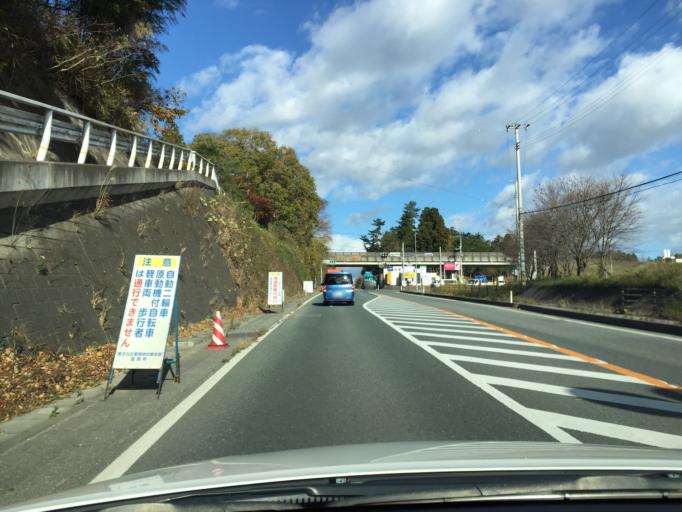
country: JP
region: Fukushima
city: Namie
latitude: 37.3464
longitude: 141.0119
